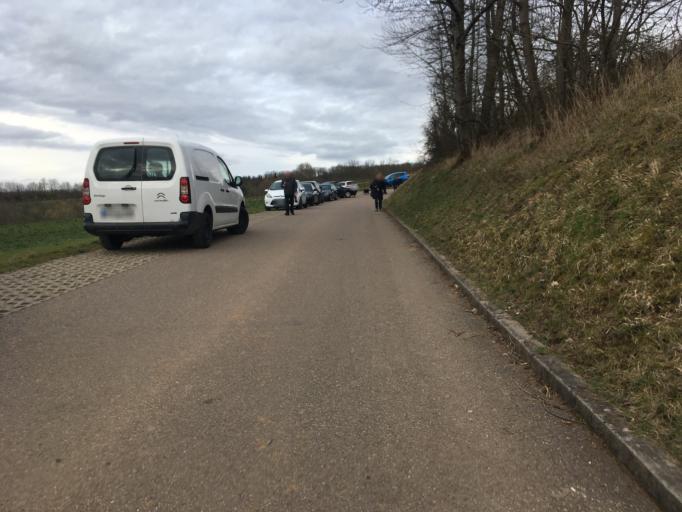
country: DE
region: Baden-Wuerttemberg
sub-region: Regierungsbezirk Stuttgart
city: Bretzfeld
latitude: 49.1625
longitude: 9.4609
